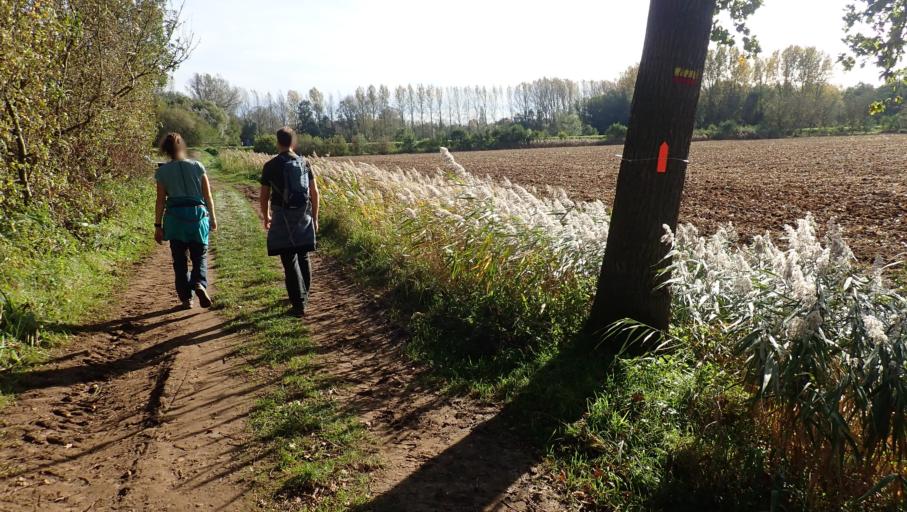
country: BE
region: Flanders
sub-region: Provincie Oost-Vlaanderen
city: Stekene
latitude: 51.1781
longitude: 4.0076
